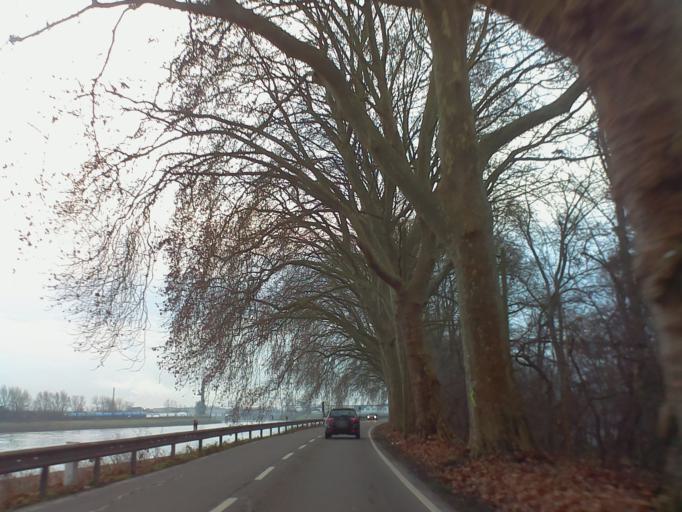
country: DE
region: Rheinland-Pfalz
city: Altrip
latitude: 49.4391
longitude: 8.5034
